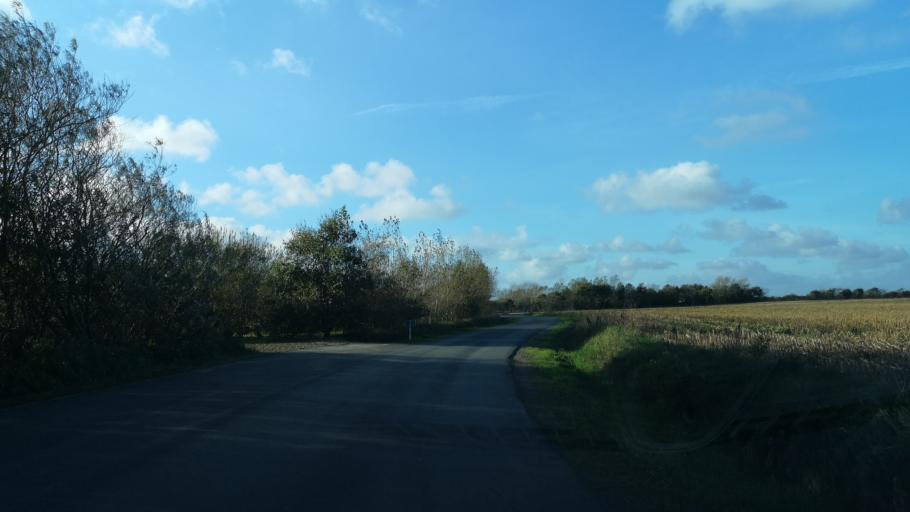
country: DK
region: Central Jutland
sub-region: Ringkobing-Skjern Kommune
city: Skjern
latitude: 55.8574
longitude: 8.3474
